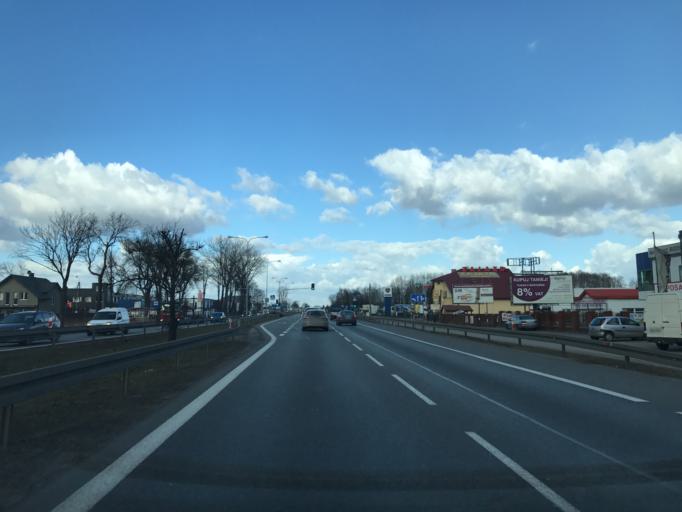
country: PL
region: Masovian Voivodeship
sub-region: Powiat wolominski
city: Slupno
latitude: 52.3775
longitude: 21.1503
